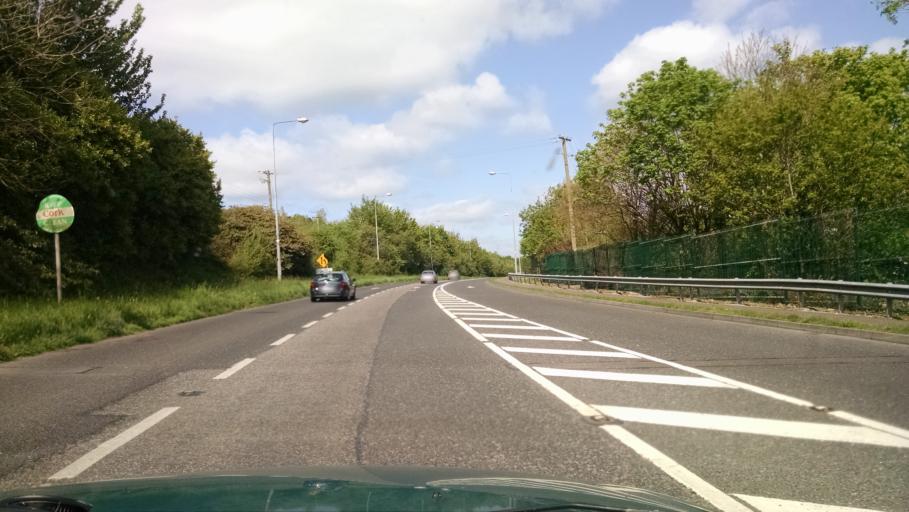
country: IE
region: Munster
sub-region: County Cork
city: Cobh
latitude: 51.8306
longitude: -8.3271
